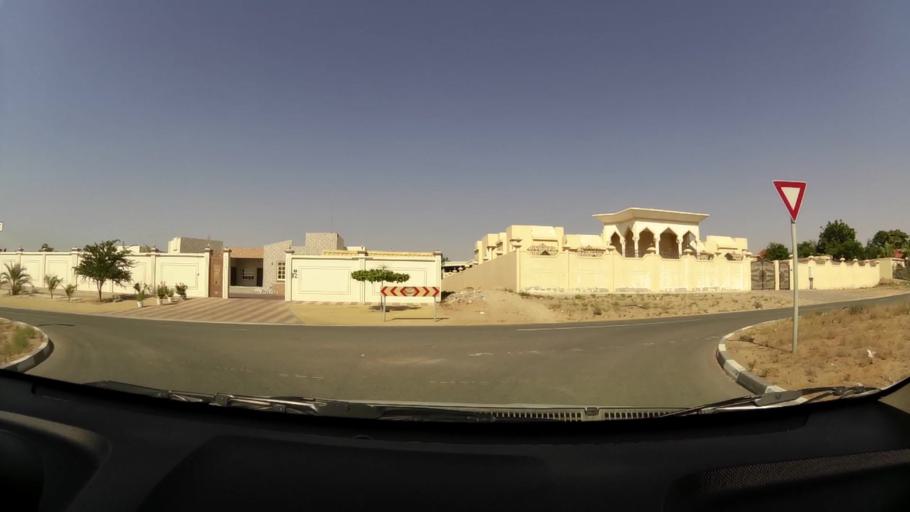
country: AE
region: Umm al Qaywayn
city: Umm al Qaywayn
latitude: 25.4927
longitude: 55.5804
